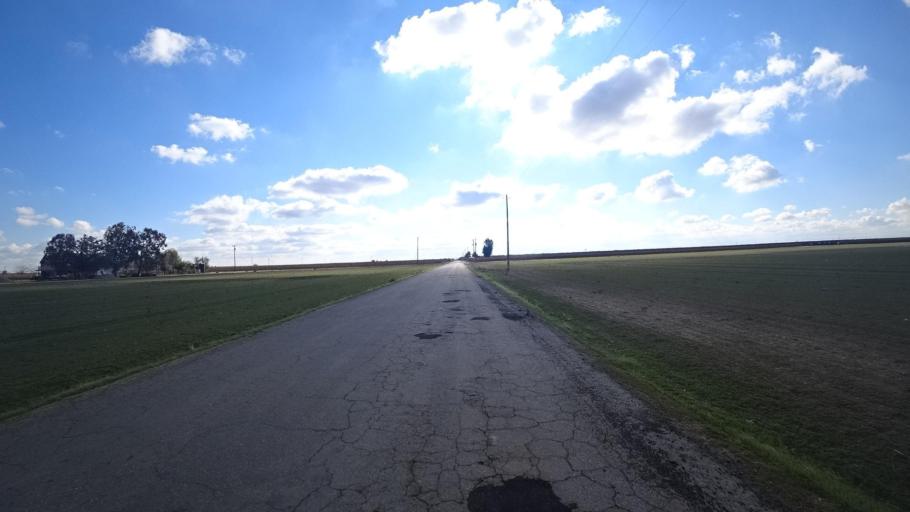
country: US
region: California
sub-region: Kern County
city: Delano
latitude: 35.7373
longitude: -119.3479
